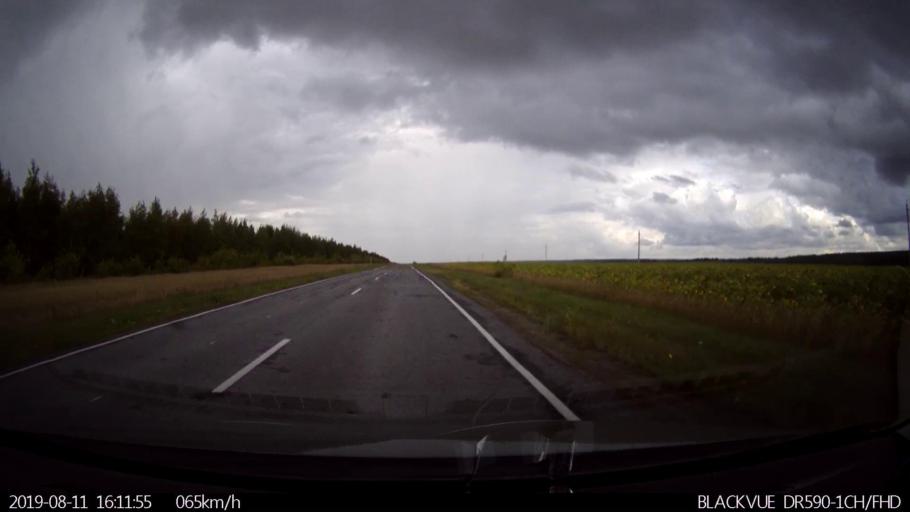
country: RU
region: Ulyanovsk
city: Ignatovka
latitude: 54.0069
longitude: 47.6423
